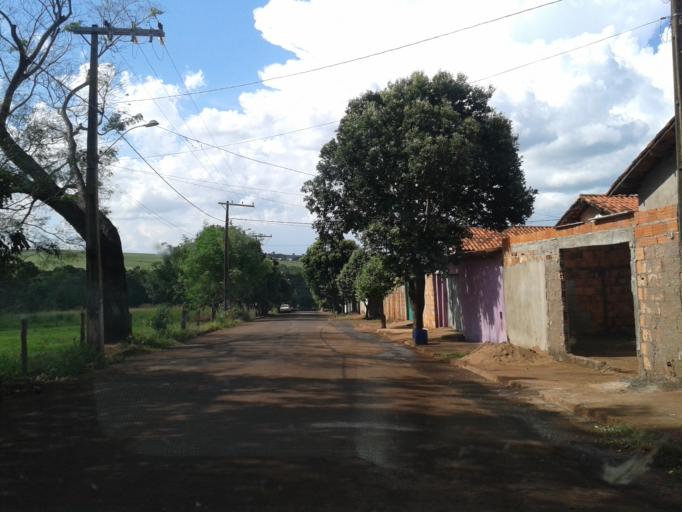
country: BR
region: Minas Gerais
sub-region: Capinopolis
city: Capinopolis
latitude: -18.6846
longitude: -49.5840
